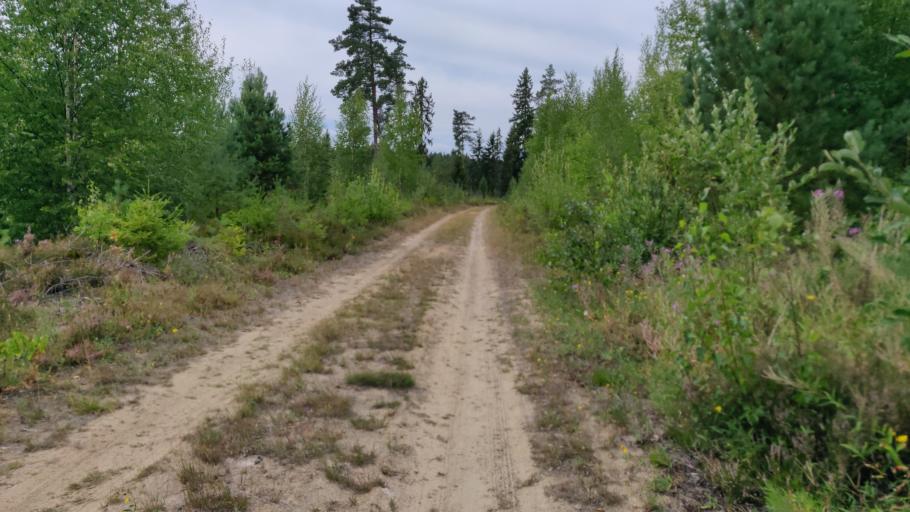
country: SE
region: Vaermland
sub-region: Hagfors Kommun
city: Hagfors
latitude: 60.0180
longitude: 13.5445
